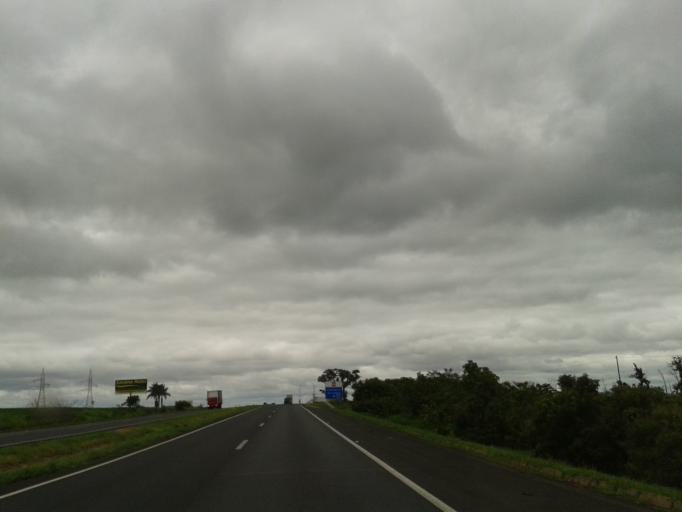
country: BR
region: Minas Gerais
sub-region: Uberlandia
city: Uberlandia
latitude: -19.0254
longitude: -48.2038
